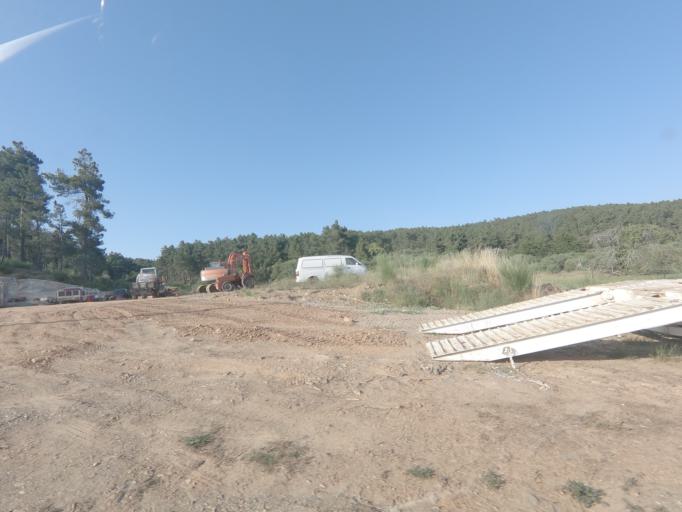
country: PT
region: Vila Real
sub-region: Sabrosa
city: Vilela
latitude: 41.2264
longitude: -7.6049
